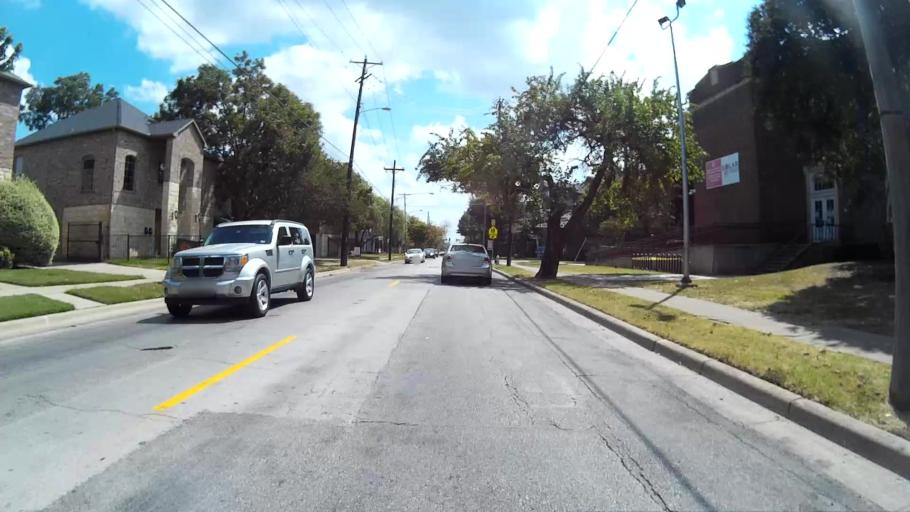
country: US
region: Texas
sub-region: Dallas County
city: Highland Park
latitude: 32.8170
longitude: -96.7811
